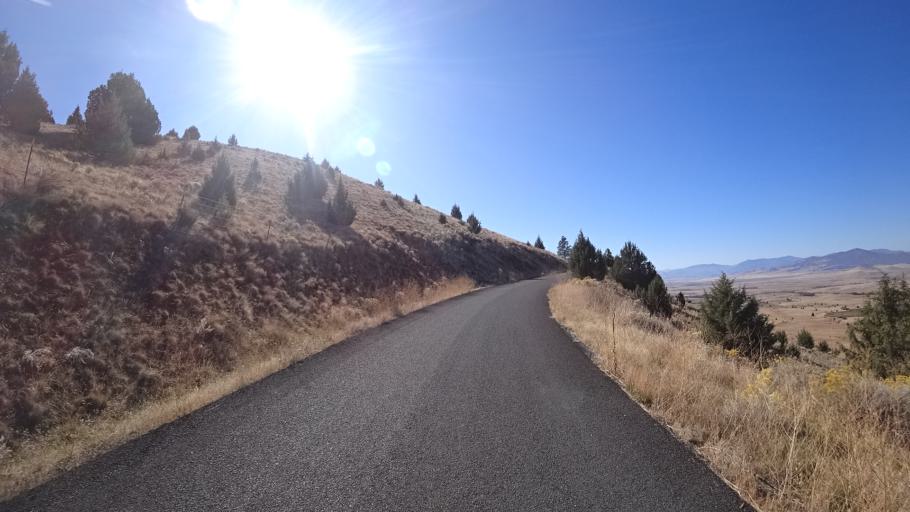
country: US
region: California
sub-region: Siskiyou County
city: Montague
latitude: 41.8268
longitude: -122.3436
